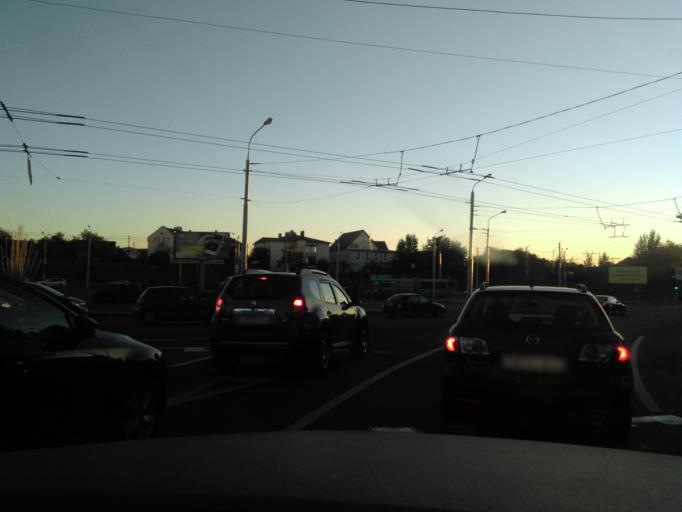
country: BY
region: Minsk
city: Minsk
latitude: 53.9077
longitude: 27.6306
